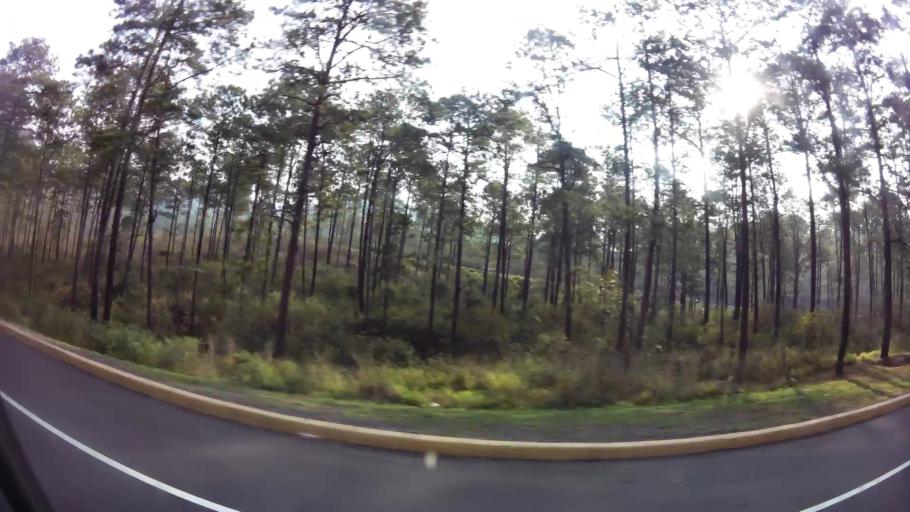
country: HN
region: Francisco Morazan
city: Zambrano
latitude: 14.2871
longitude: -87.4742
